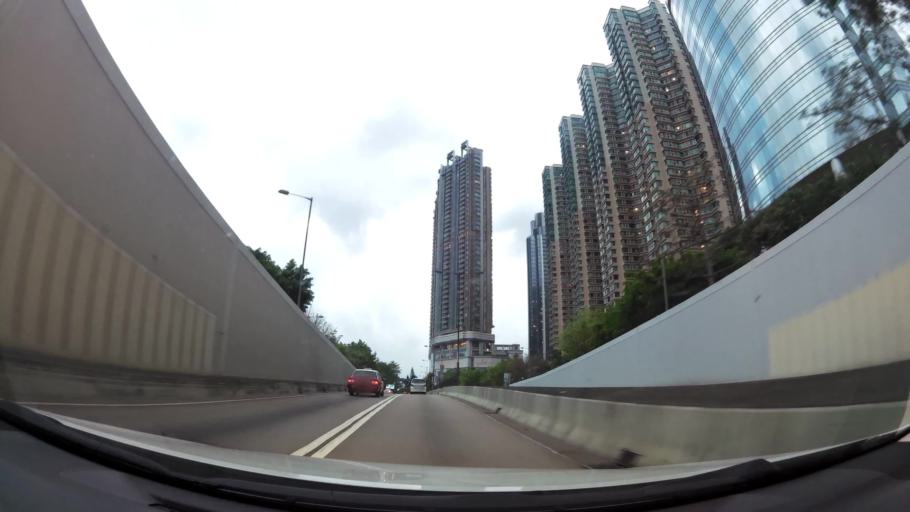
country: HK
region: Sham Shui Po
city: Sham Shui Po
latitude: 22.3172
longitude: 114.1595
